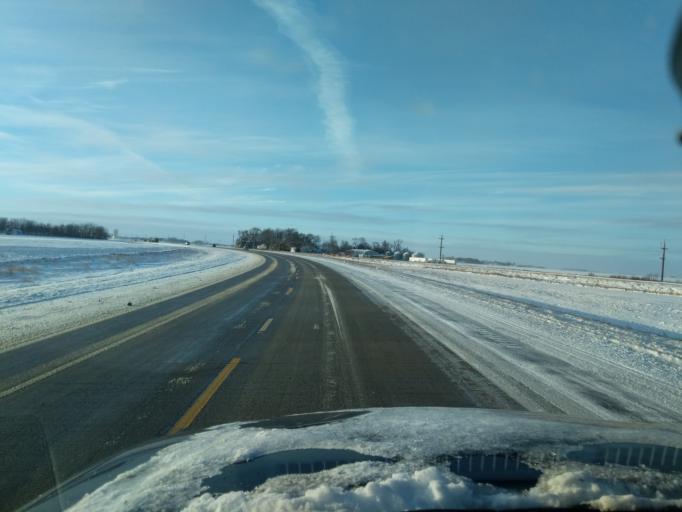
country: US
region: Minnesota
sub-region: Renville County
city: Olivia
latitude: 44.7726
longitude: -94.9435
